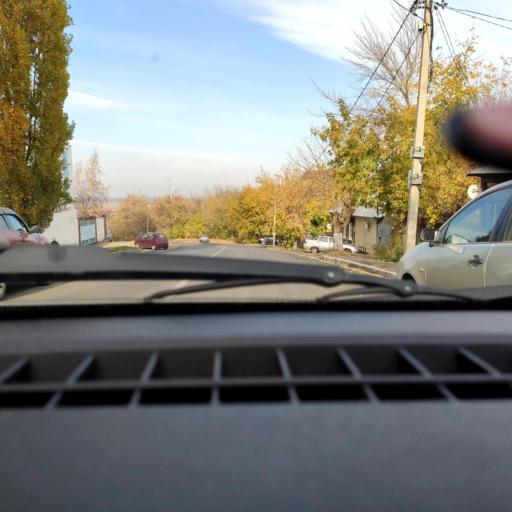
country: RU
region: Bashkortostan
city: Ufa
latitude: 54.7373
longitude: 55.9337
